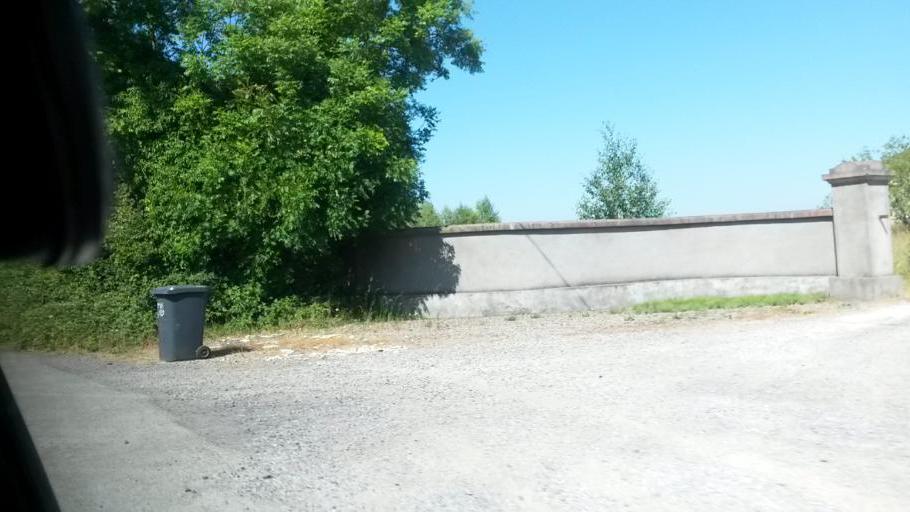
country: IE
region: Leinster
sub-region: Fingal County
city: Swords
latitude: 53.4863
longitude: -6.2852
